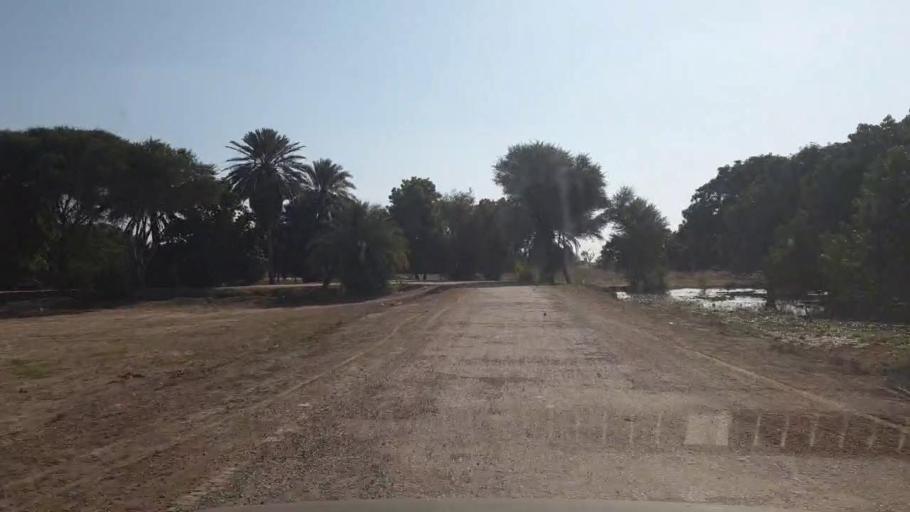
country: PK
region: Sindh
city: Tando Allahyar
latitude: 25.4311
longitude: 68.6822
